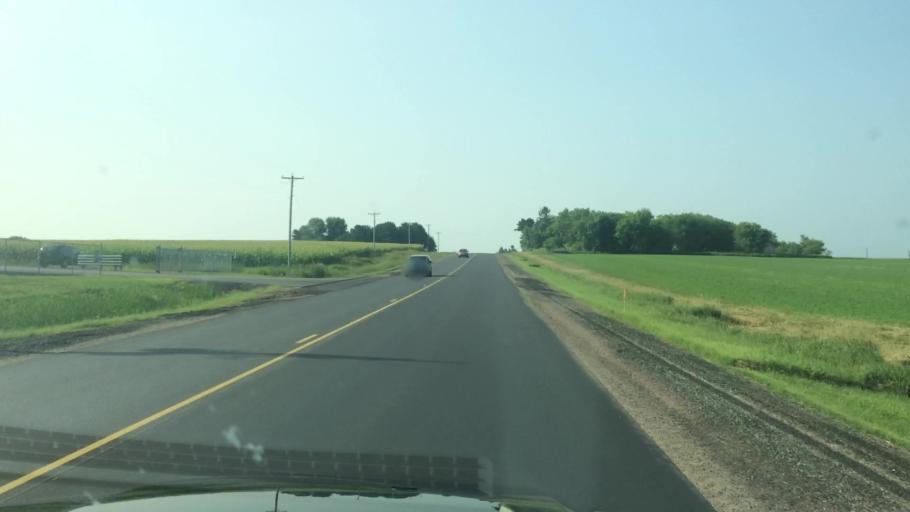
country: US
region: Wisconsin
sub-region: Marathon County
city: Stratford
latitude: 44.8918
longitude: -90.0789
